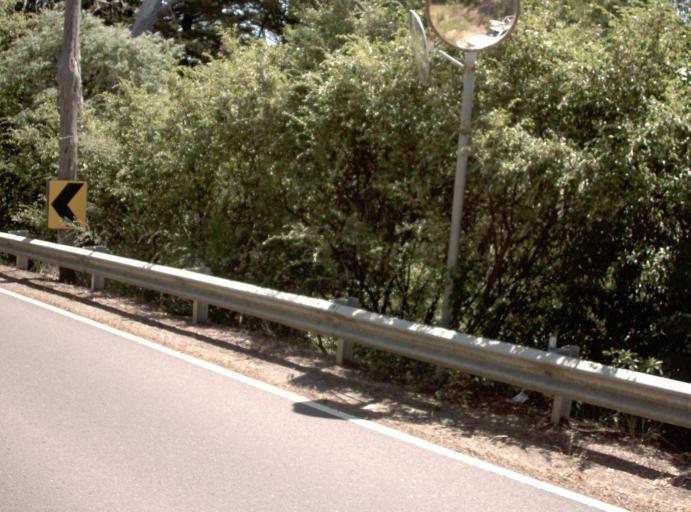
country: AU
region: Victoria
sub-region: Yarra Ranges
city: Kalorama
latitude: -37.8125
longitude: 145.3631
